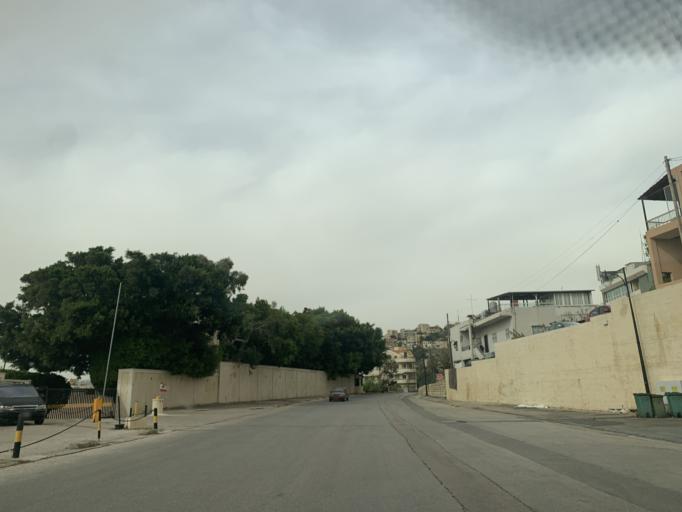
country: LB
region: Mont-Liban
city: Jbail
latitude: 34.0937
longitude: 35.6512
